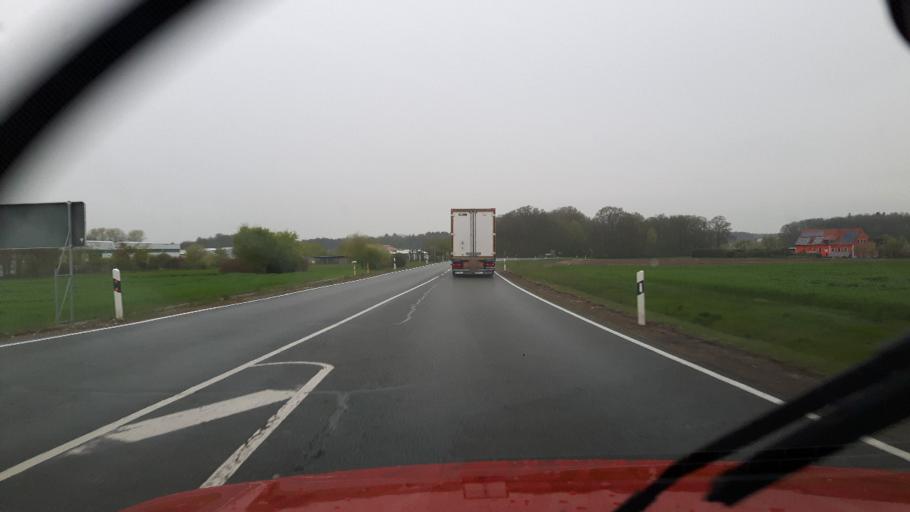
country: DE
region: Bavaria
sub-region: Regierungsbezirk Mittelfranken
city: Merkendorf
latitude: 49.2002
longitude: 10.6882
